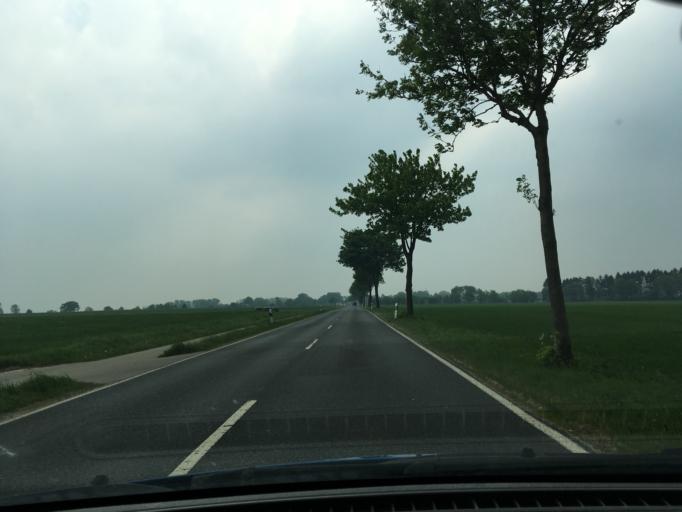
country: DE
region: Lower Saxony
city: Buchholz in der Nordheide
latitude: 53.3919
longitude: 9.8598
